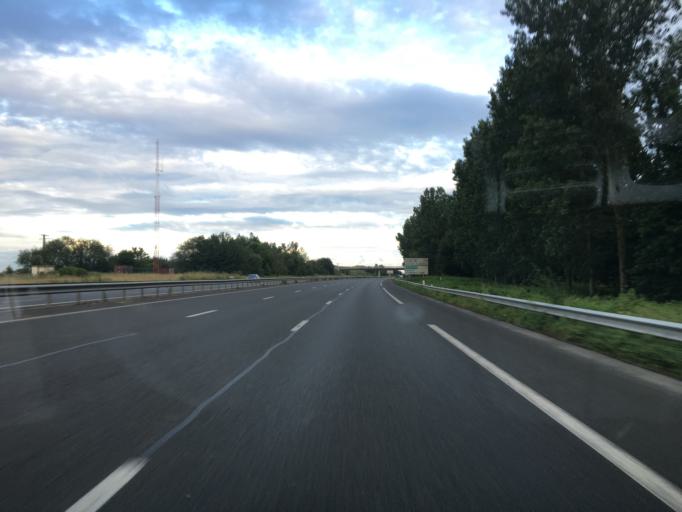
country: FR
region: Ile-de-France
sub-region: Departement de Seine-et-Marne
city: Moisenay
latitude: 48.5822
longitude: 2.7351
